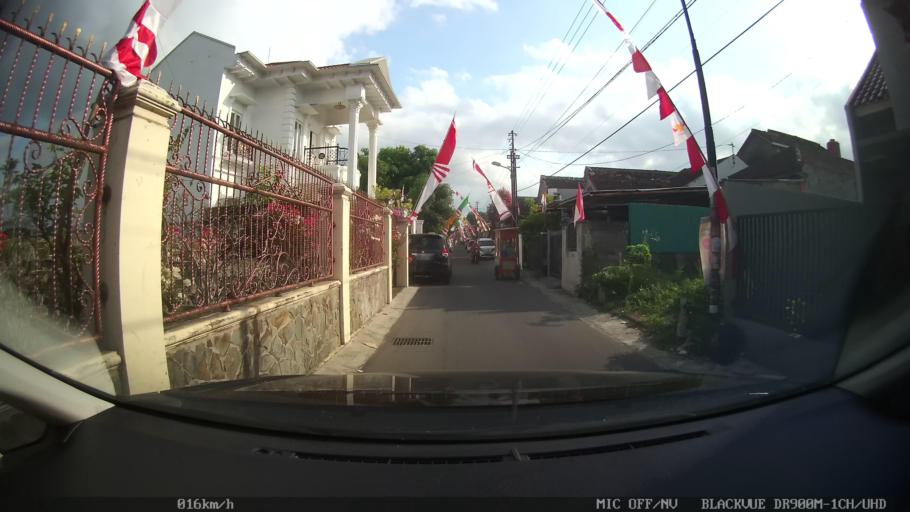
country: ID
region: Daerah Istimewa Yogyakarta
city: Kasihan
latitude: -7.8172
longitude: 110.3589
